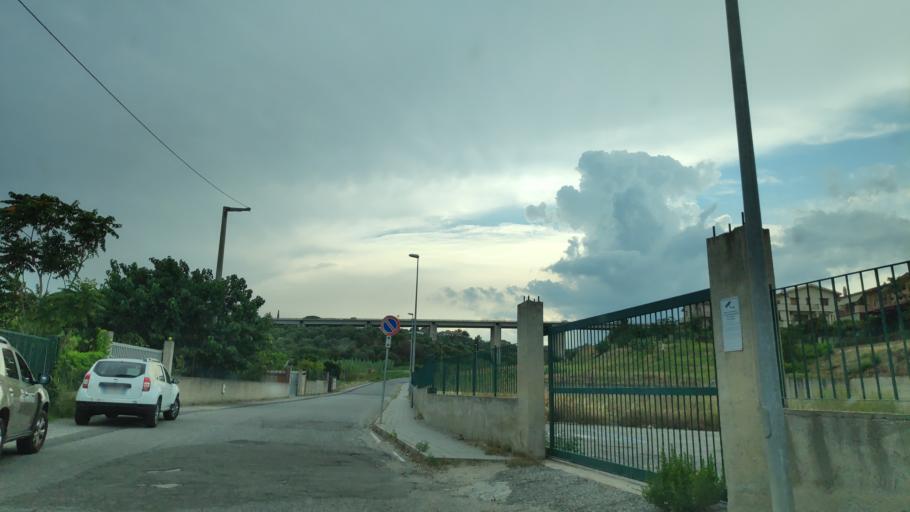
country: IT
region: Calabria
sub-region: Provincia di Catanzaro
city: Soverato Marina
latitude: 38.6837
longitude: 16.5475
